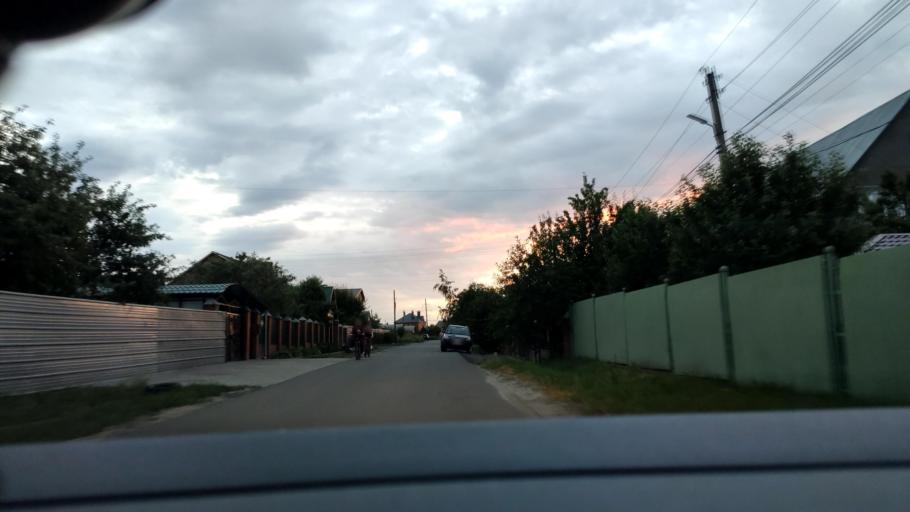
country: RU
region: Voronezj
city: Semiluki
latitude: 51.7037
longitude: 39.0268
